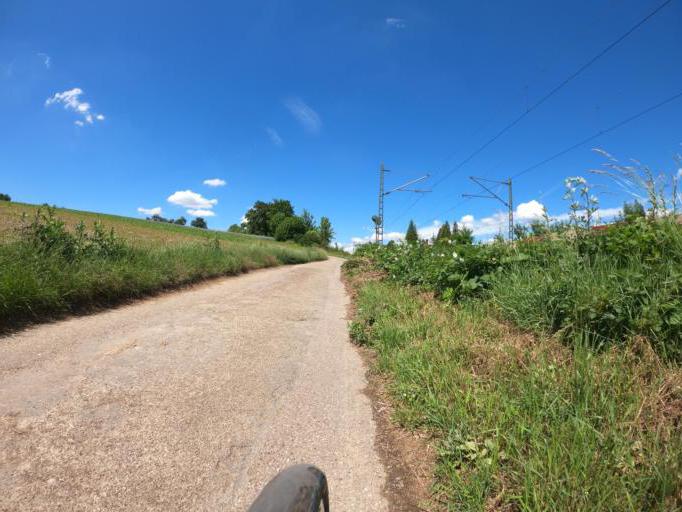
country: DE
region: Baden-Wuerttemberg
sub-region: Regierungsbezirk Stuttgart
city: Sersheim
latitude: 48.9610
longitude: 9.0529
